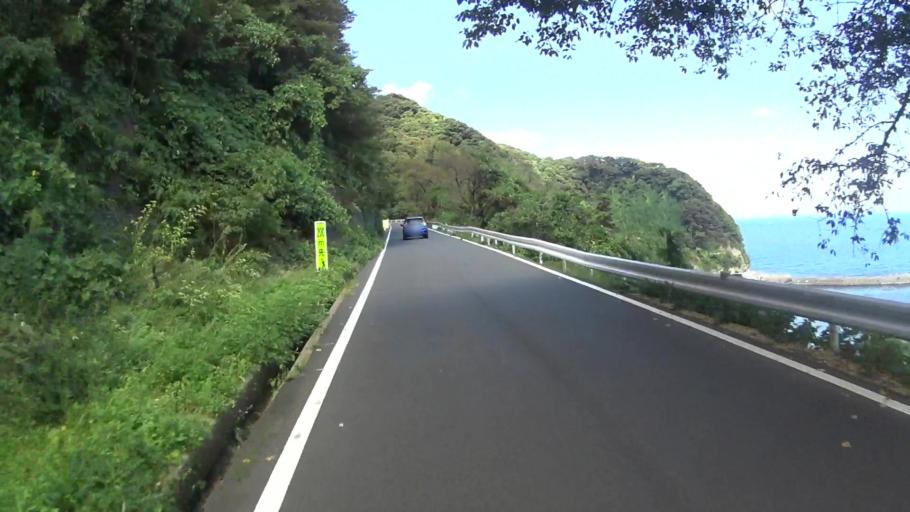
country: JP
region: Kyoto
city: Miyazu
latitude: 35.7540
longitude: 135.2499
